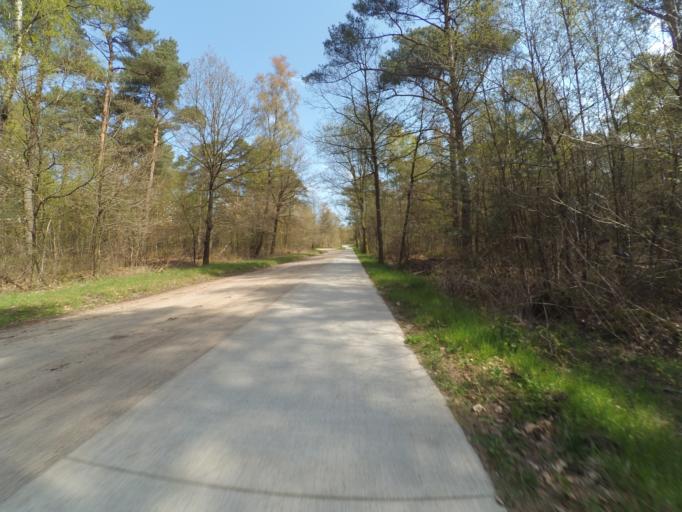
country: NL
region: Gelderland
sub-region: Gemeente Oldebroek
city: Oldebroek
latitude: 52.3800
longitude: 5.9120
